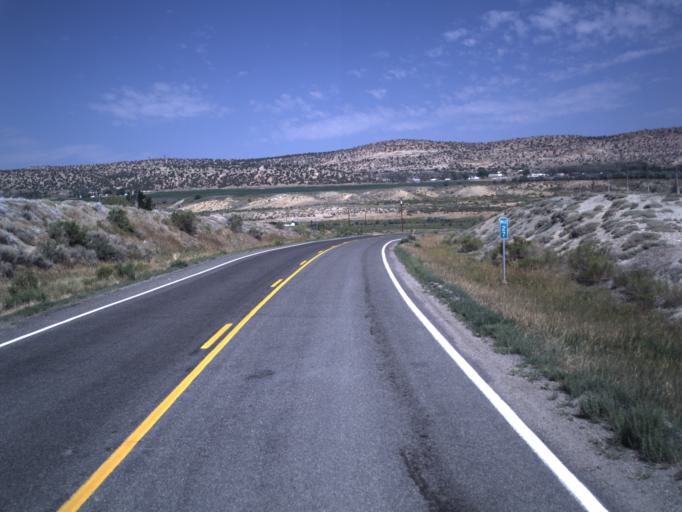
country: US
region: Utah
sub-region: Daggett County
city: Manila
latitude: 40.9740
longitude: -109.7204
